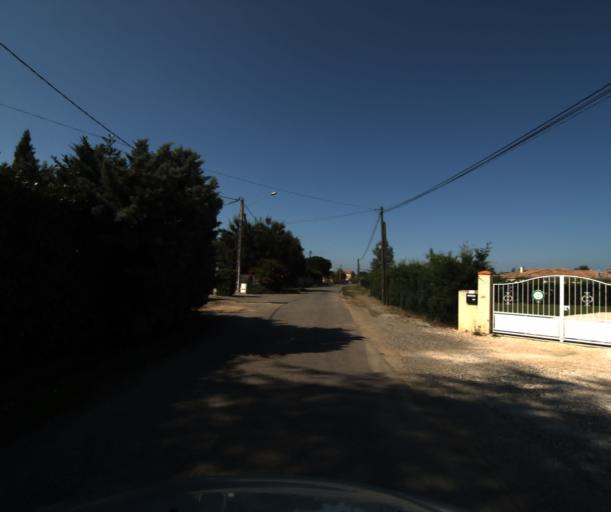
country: FR
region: Midi-Pyrenees
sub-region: Departement de la Haute-Garonne
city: Lacasse
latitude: 43.3877
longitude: 1.2585
